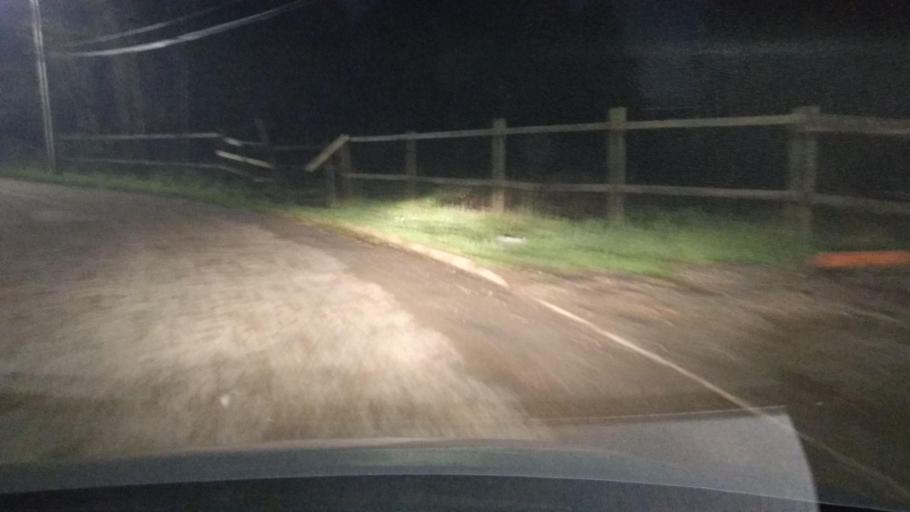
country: CL
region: Los Rios
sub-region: Provincia de Valdivia
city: Valdivia
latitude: -39.8176
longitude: -73.2553
